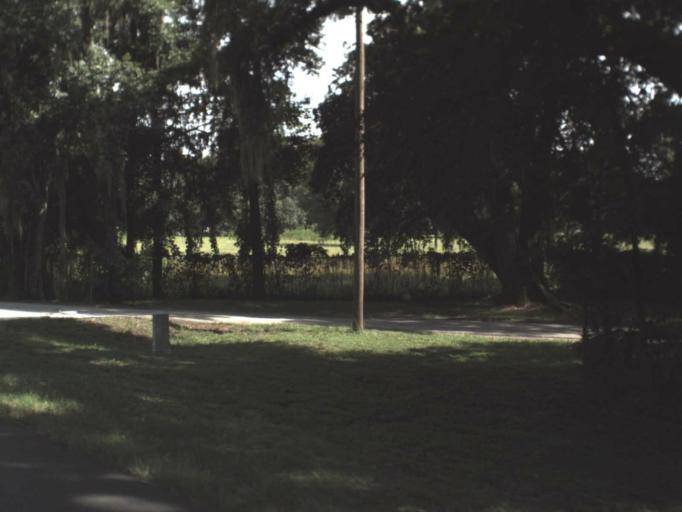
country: US
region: Florida
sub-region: Pasco County
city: Crystal Springs
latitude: 28.1952
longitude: -82.1667
